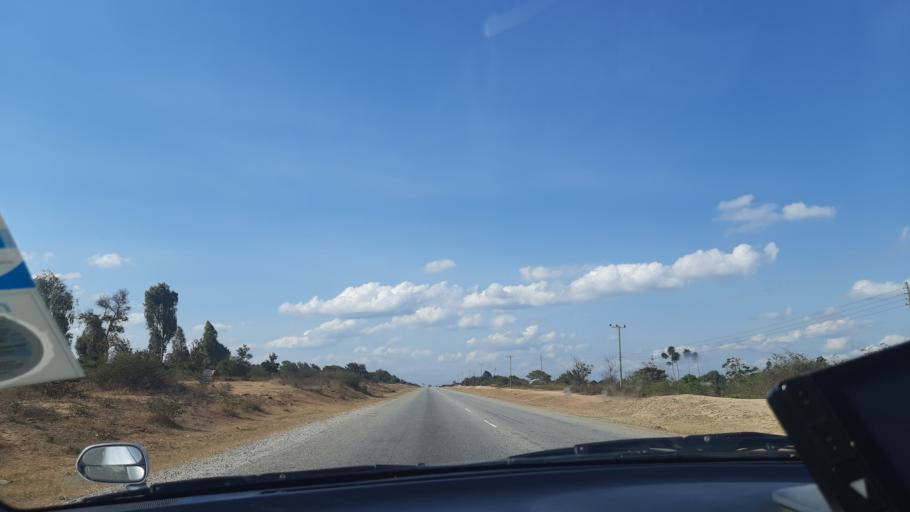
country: TZ
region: Singida
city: Itigi
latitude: -5.5494
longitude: 34.6654
